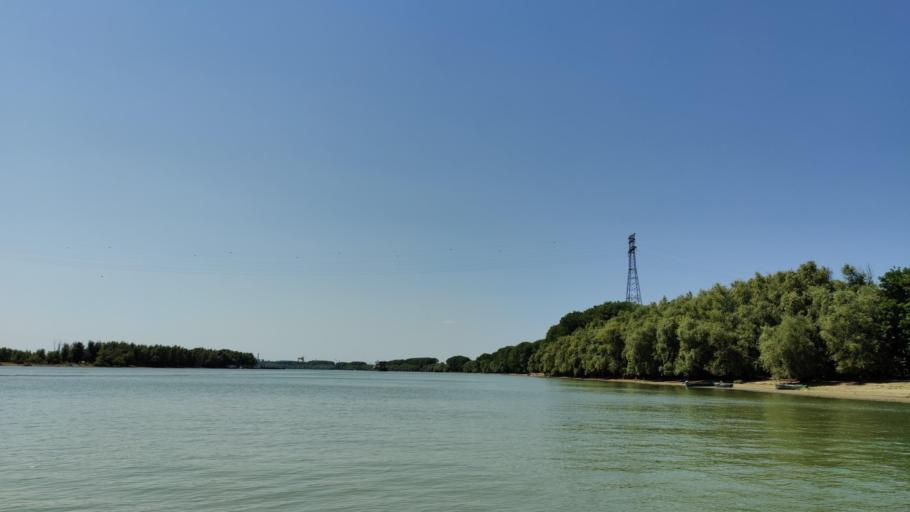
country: RO
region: Tulcea
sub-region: Municipiul Tulcea
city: Tulcea
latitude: 45.2039
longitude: 28.8504
